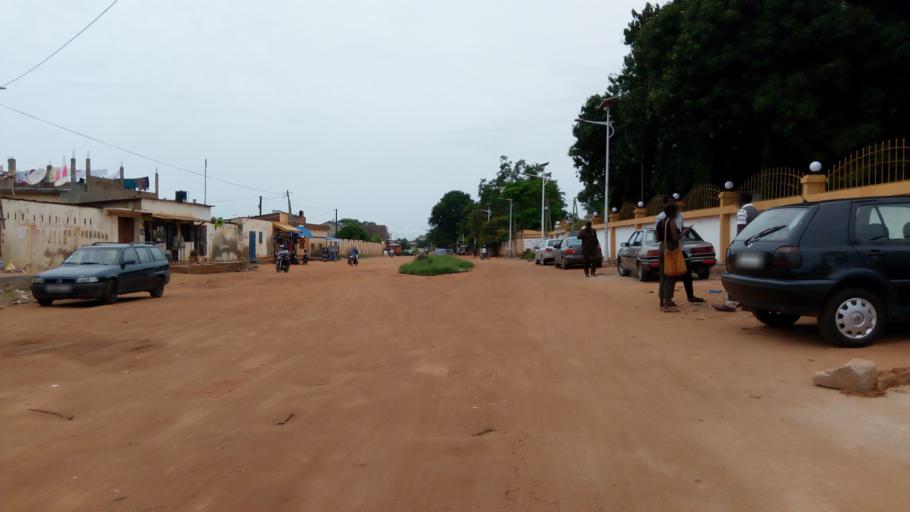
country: TG
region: Maritime
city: Lome
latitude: 6.1605
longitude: 1.2186
